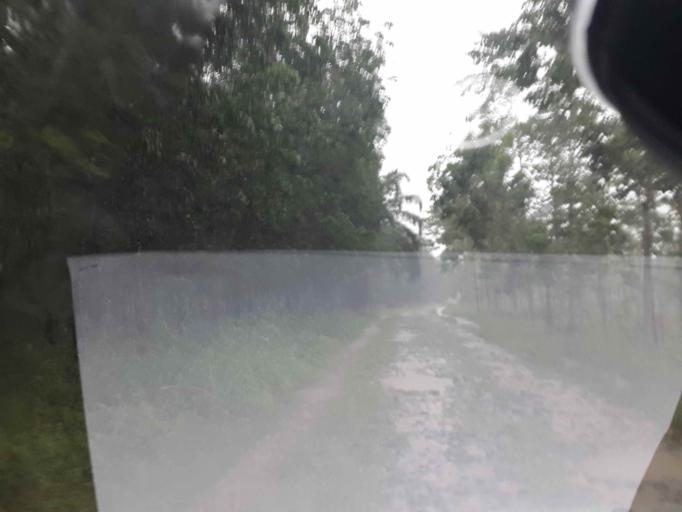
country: ID
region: Lampung
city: Kedaton
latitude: -5.3921
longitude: 105.3397
